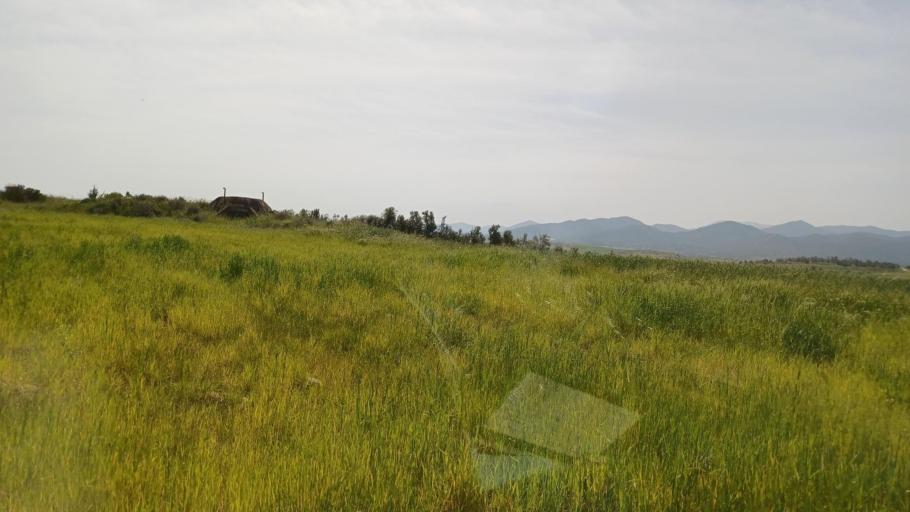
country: CY
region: Lefkosia
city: Astromeritis
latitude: 35.1051
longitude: 32.9640
